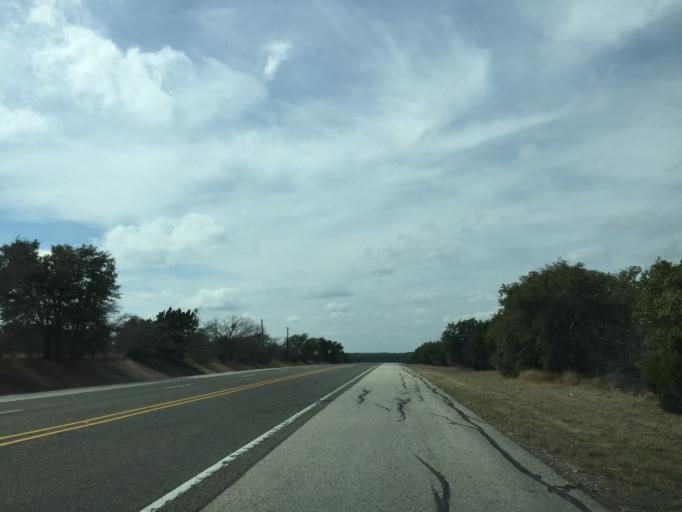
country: US
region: Texas
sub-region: Llano County
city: Horseshoe Bay
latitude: 30.5136
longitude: -98.3678
